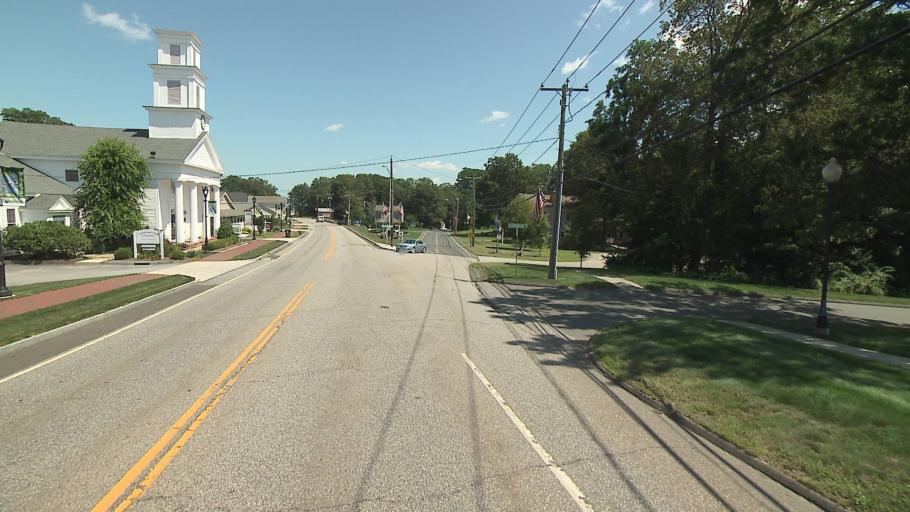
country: US
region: Connecticut
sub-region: Hartford County
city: Collinsville
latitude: 41.7690
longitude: -72.9665
